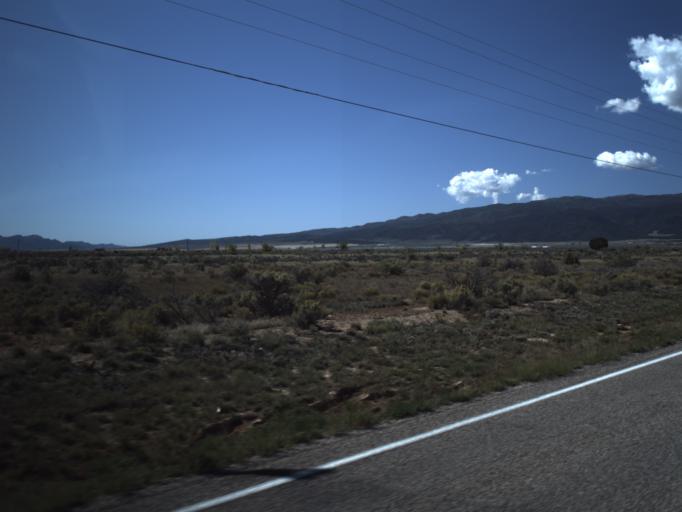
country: US
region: Utah
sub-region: Iron County
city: Cedar City
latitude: 37.6730
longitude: -113.1866
